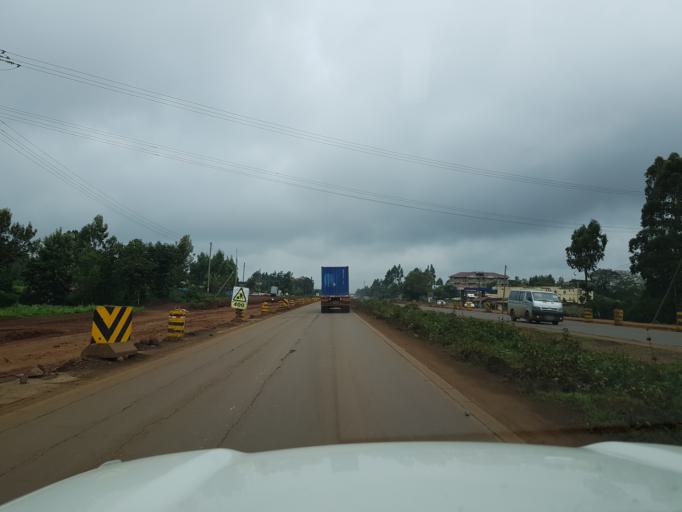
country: KE
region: Kiambu
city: Limuru
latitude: -1.1374
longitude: 36.6359
